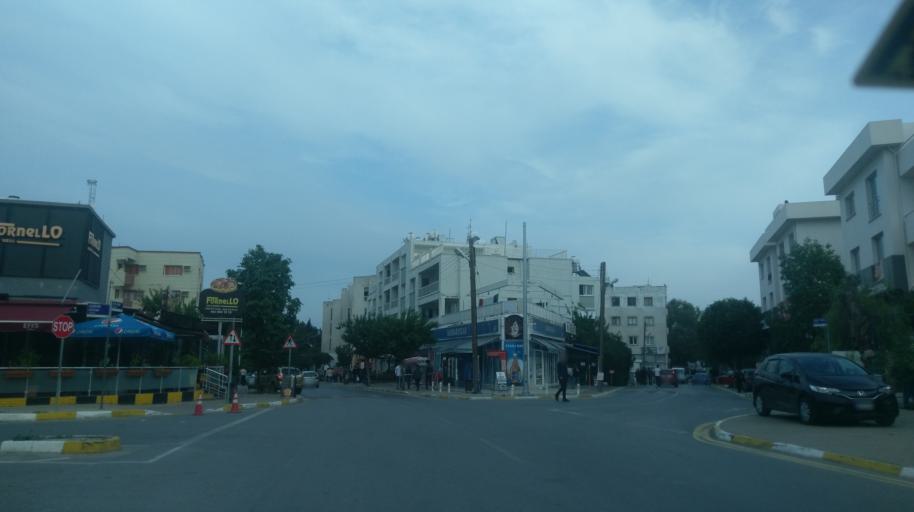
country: CY
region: Keryneia
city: Kyrenia
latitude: 35.3375
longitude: 33.3112
